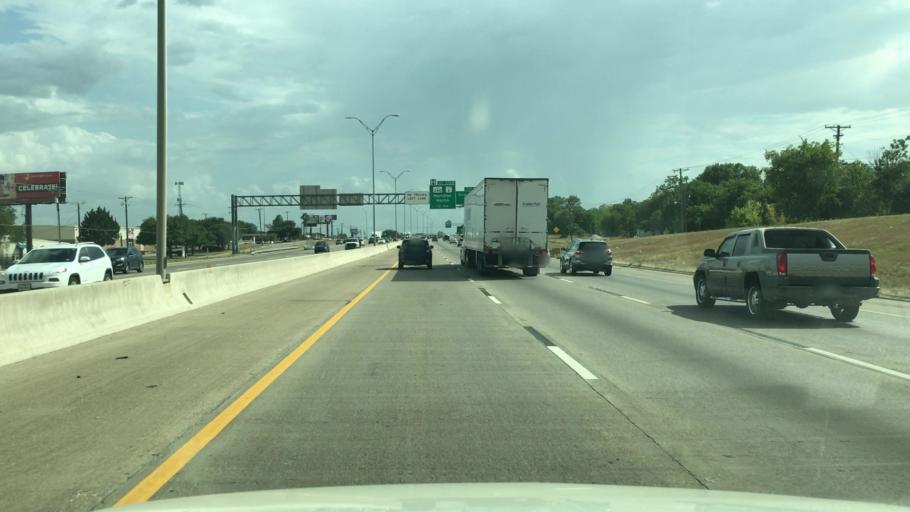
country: US
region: Texas
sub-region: McLennan County
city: Beverly
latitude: 31.5155
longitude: -97.1386
